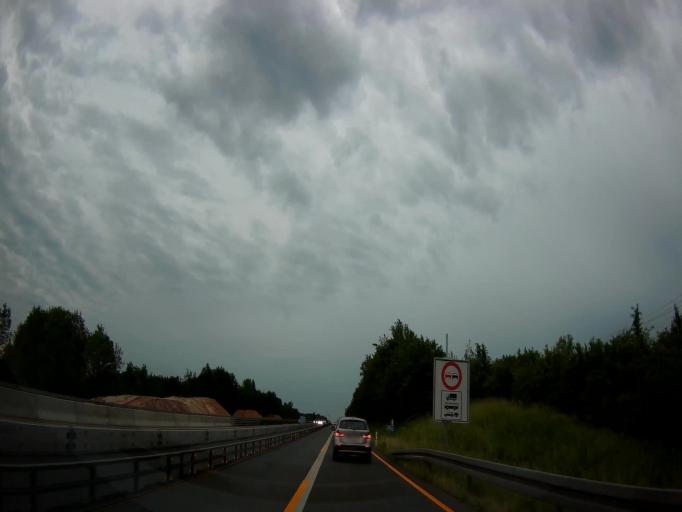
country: DE
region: Bavaria
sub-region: Regierungsbezirk Mittelfranken
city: Allersberg
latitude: 49.2389
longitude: 11.2189
